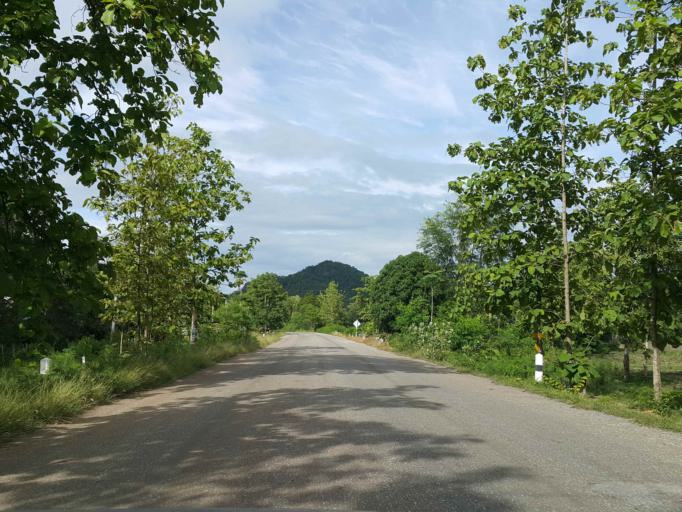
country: TH
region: Sukhothai
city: Thung Saliam
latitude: 17.2640
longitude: 99.5342
